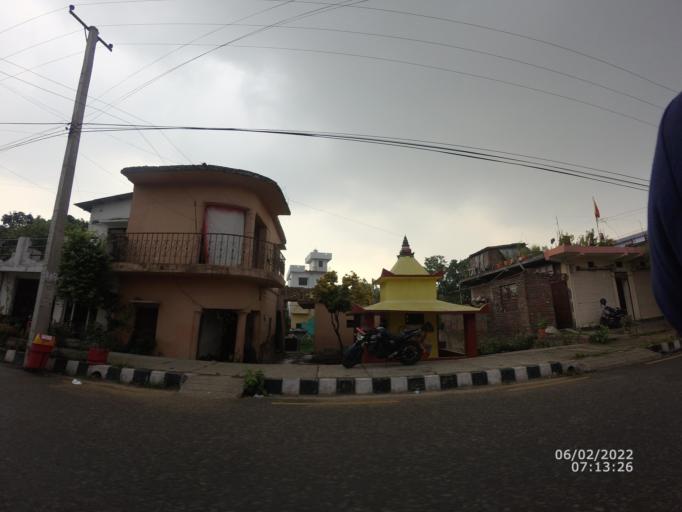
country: NP
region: Western Region
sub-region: Lumbini Zone
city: Bhairahawa
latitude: 27.4817
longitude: 83.4425
